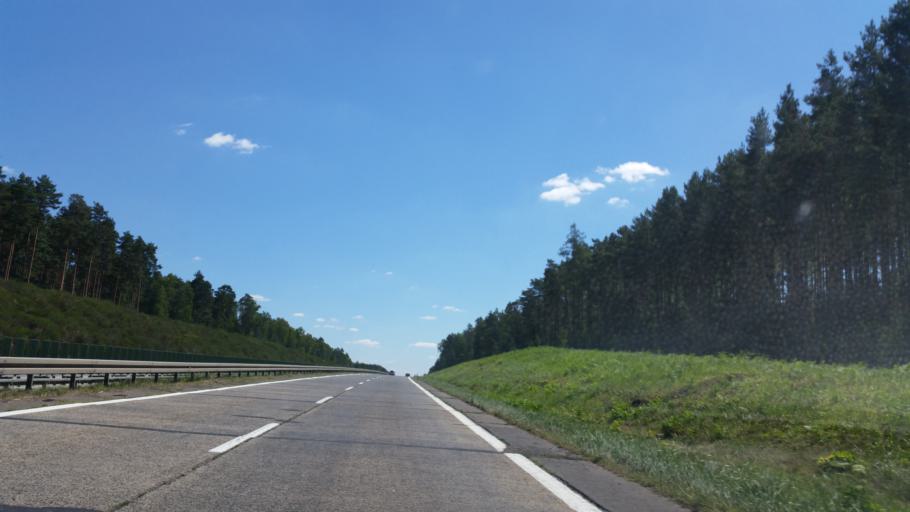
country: PL
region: Lubusz
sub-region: Powiat zaganski
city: Malomice
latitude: 51.4125
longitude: 15.4951
